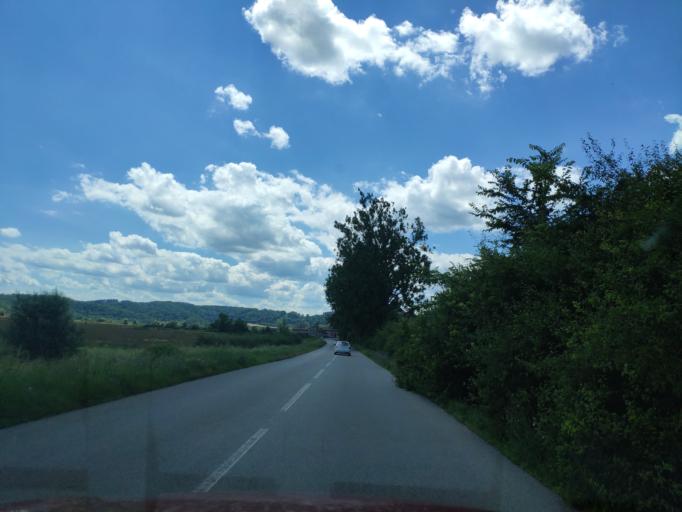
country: HU
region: Borsod-Abauj-Zemplen
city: Ozd
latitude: 48.3066
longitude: 20.2464
